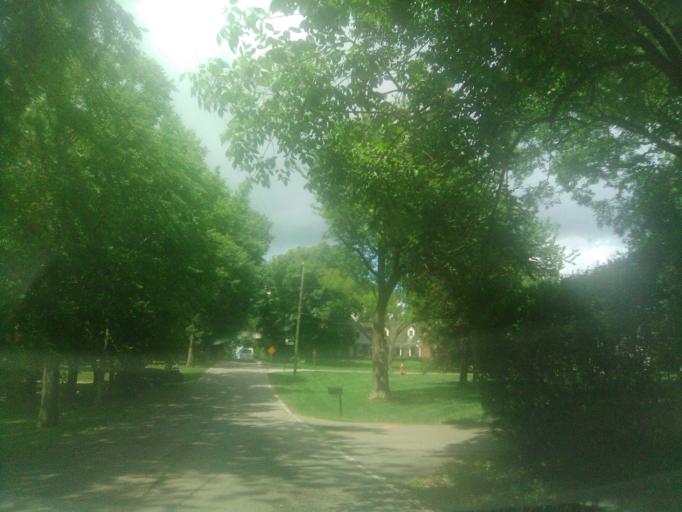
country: US
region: Tennessee
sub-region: Davidson County
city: Belle Meade
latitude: 36.1026
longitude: -86.8491
